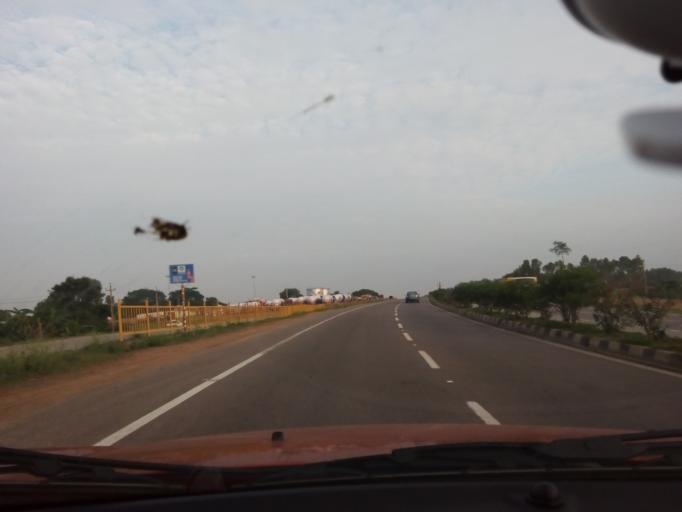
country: IN
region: Karnataka
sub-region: Ramanagara
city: Magadi
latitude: 13.0696
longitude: 77.2378
